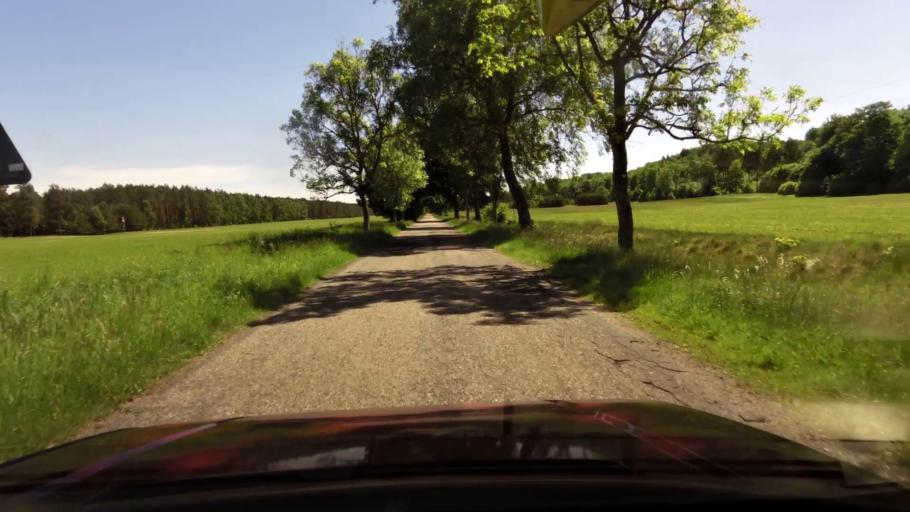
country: PL
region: West Pomeranian Voivodeship
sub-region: Powiat koszalinski
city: Bobolice
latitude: 54.0329
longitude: 16.6186
